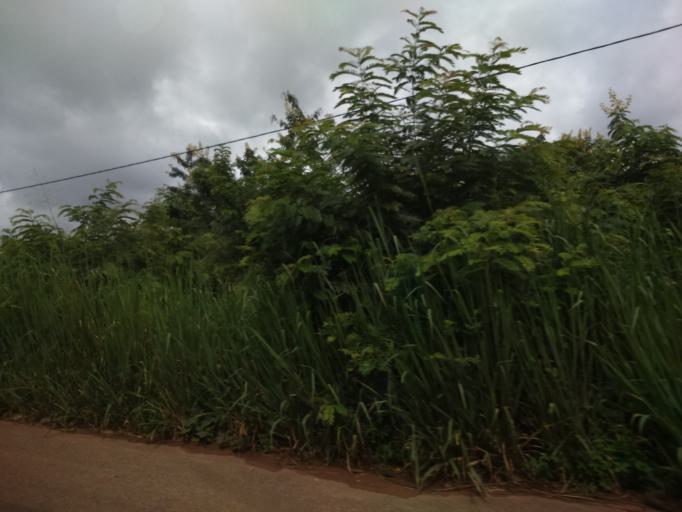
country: CI
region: Moyen-Comoe
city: Abengourou
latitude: 6.6297
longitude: -3.7105
